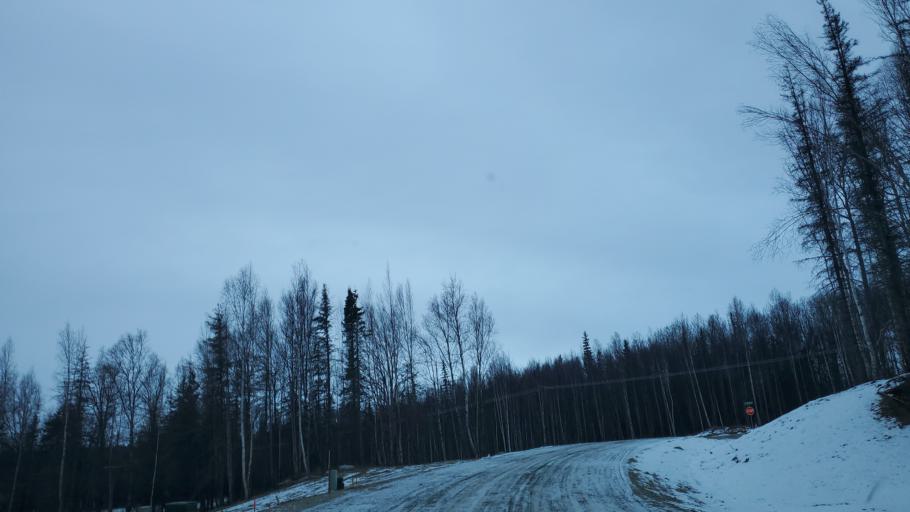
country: US
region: Alaska
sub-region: Matanuska-Susitna Borough
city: Gateway
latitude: 61.6564
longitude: -149.2361
